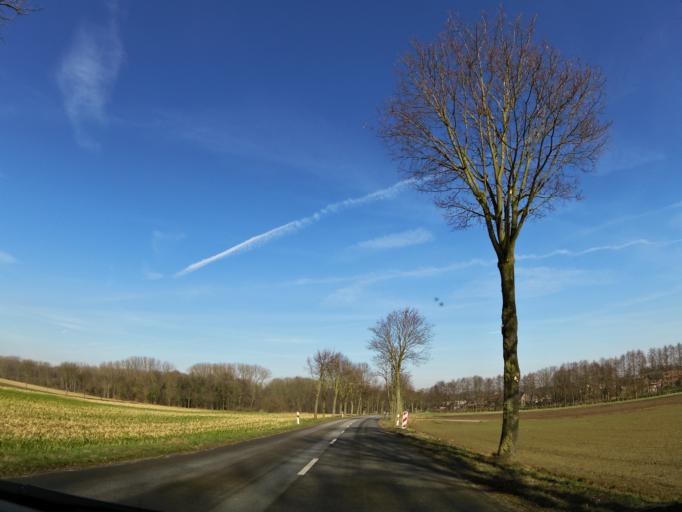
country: NL
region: Limburg
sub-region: Gemeente Onderbanken
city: Merkelbeek
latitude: 50.9890
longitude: 5.9422
